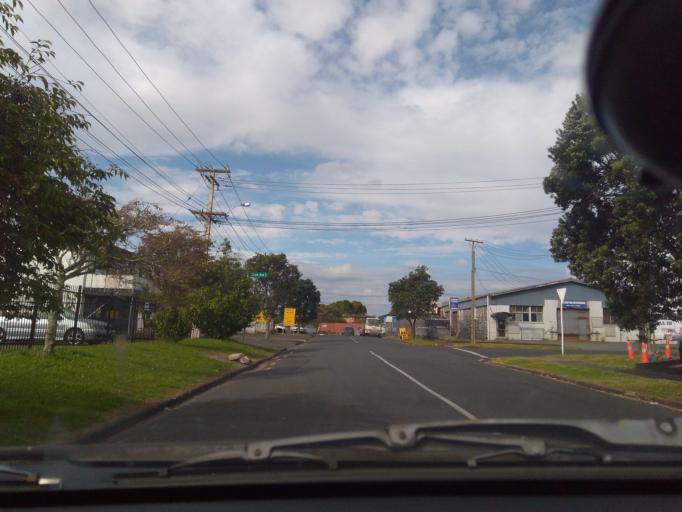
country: NZ
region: Auckland
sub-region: Auckland
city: Waitakere
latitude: -36.9029
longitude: 174.6853
